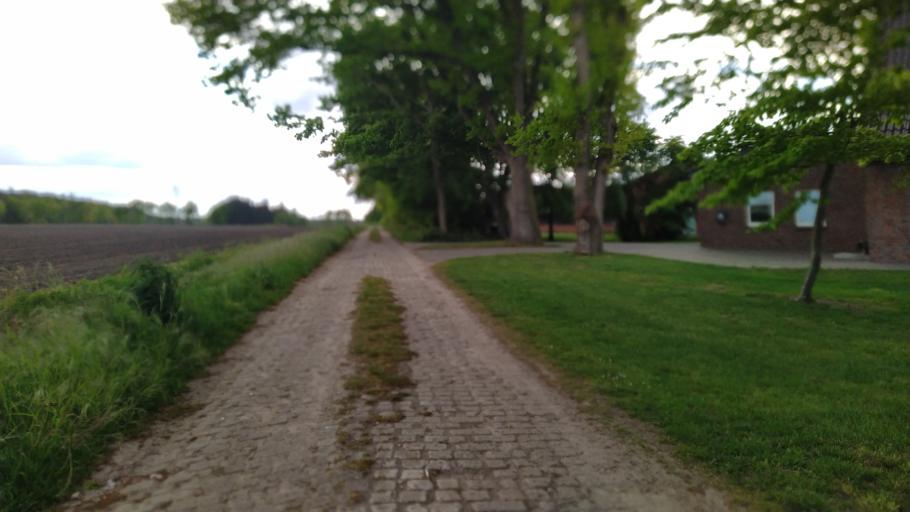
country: DE
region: Lower Saxony
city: Brest
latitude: 53.4232
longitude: 9.3884
